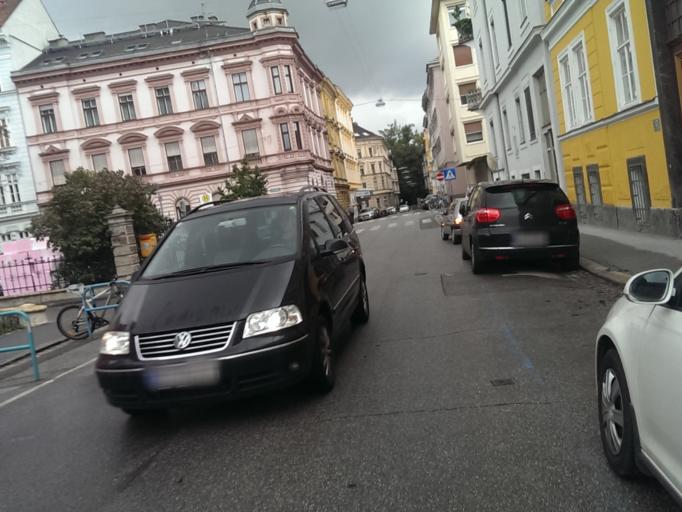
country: AT
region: Styria
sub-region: Graz Stadt
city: Graz
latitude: 47.0696
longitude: 15.4504
